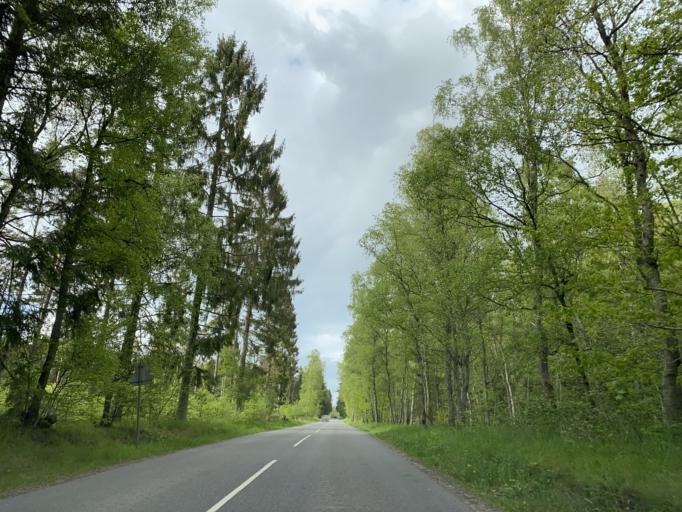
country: DK
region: Central Jutland
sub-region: Skanderborg Kommune
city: Ry
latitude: 56.0603
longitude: 9.6915
